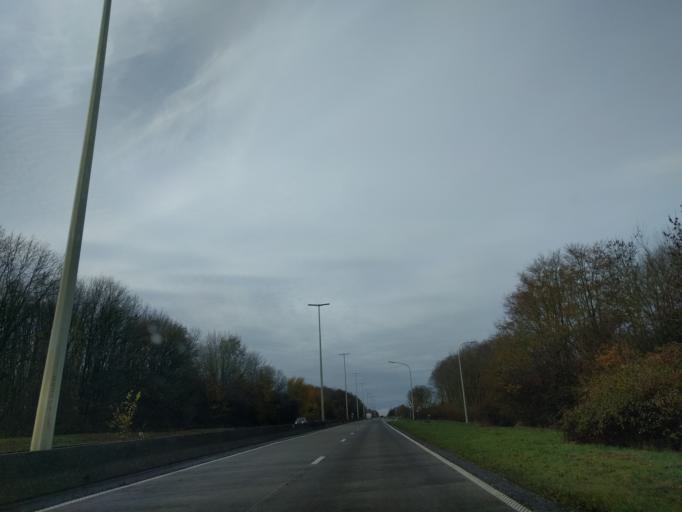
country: BE
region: Wallonia
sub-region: Province de Namur
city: Dinant
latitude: 50.2401
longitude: 4.9712
